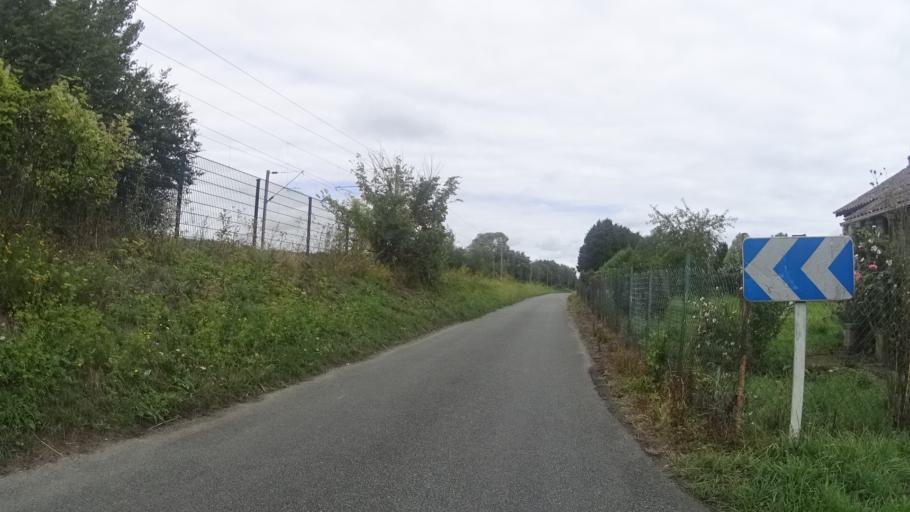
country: FR
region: Picardie
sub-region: Departement de l'Oise
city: Chiry-Ourscamp
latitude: 49.5286
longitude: 2.9522
